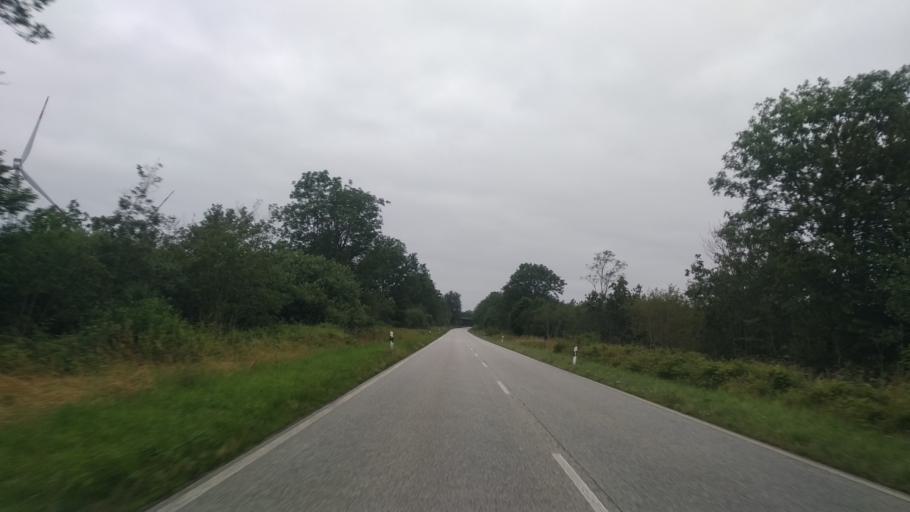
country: DE
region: Schleswig-Holstein
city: Sieverstedt
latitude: 54.6448
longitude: 9.4563
